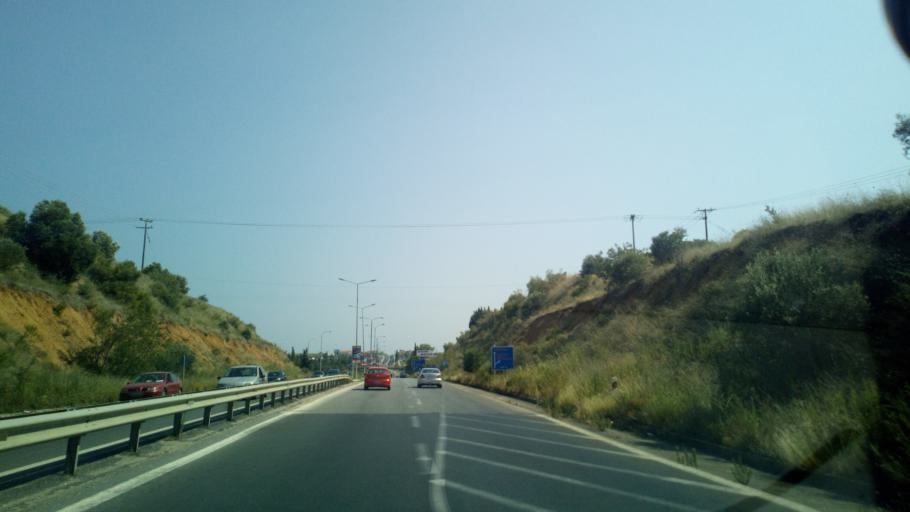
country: GR
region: Central Macedonia
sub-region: Nomos Chalkidikis
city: Nea Moudhania
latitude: 40.2459
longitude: 23.2964
